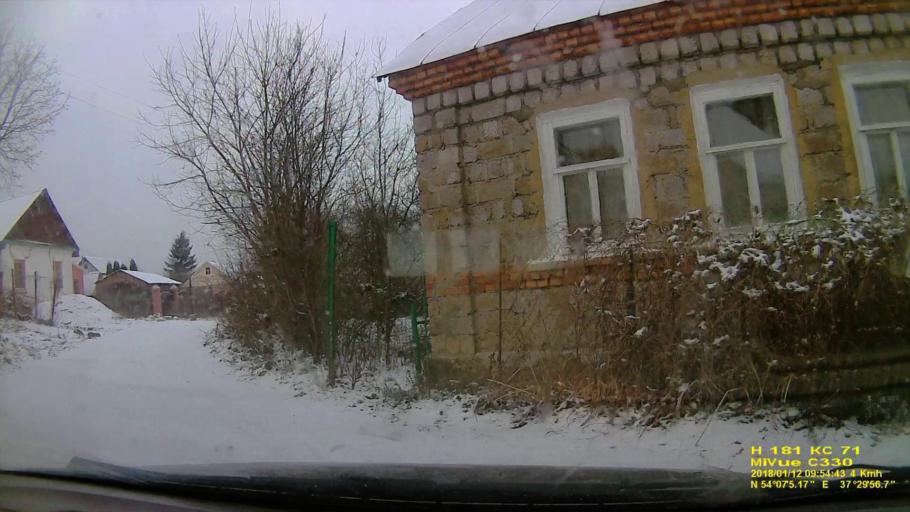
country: RU
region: Tula
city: Kosaya Gora
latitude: 54.1181
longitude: 37.4991
